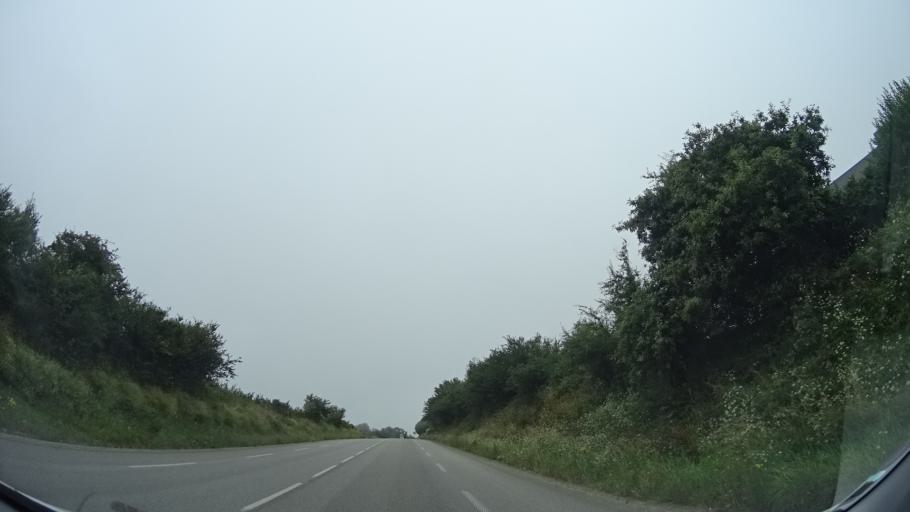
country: FR
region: Lower Normandy
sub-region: Departement de la Manche
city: Les Pieux
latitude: 49.5176
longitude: -1.8074
